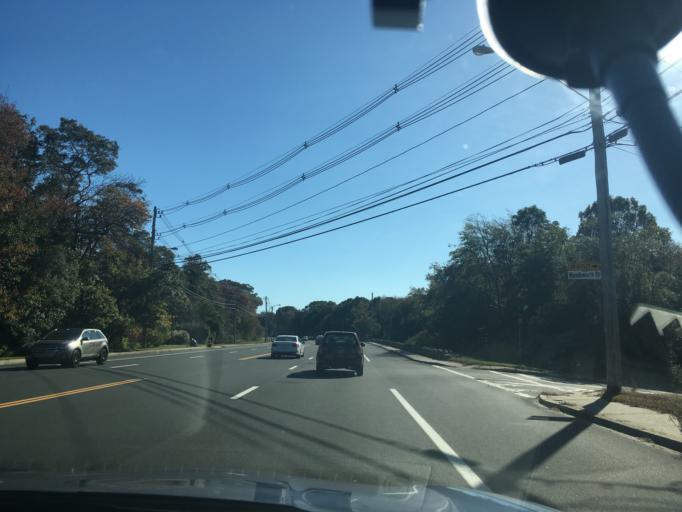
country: US
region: Rhode Island
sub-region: Washington County
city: Narragansett Pier
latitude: 41.4232
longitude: -71.4814
